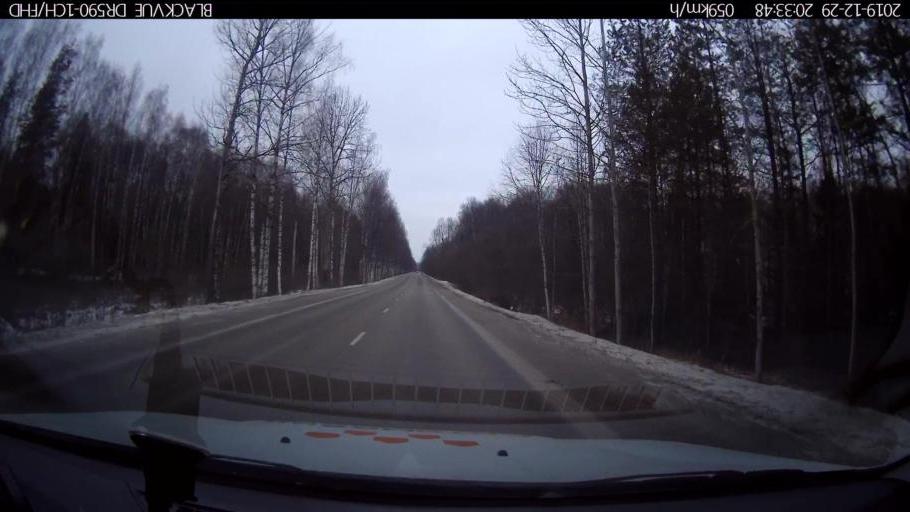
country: RU
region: Nizjnij Novgorod
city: Afonino
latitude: 56.1825
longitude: 44.0474
